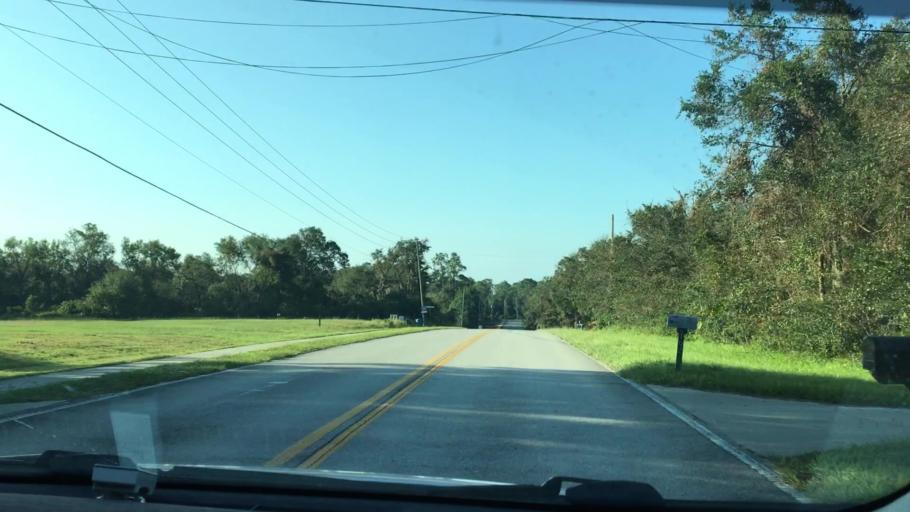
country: US
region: Florida
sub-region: Volusia County
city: Deltona
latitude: 28.8646
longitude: -81.2318
